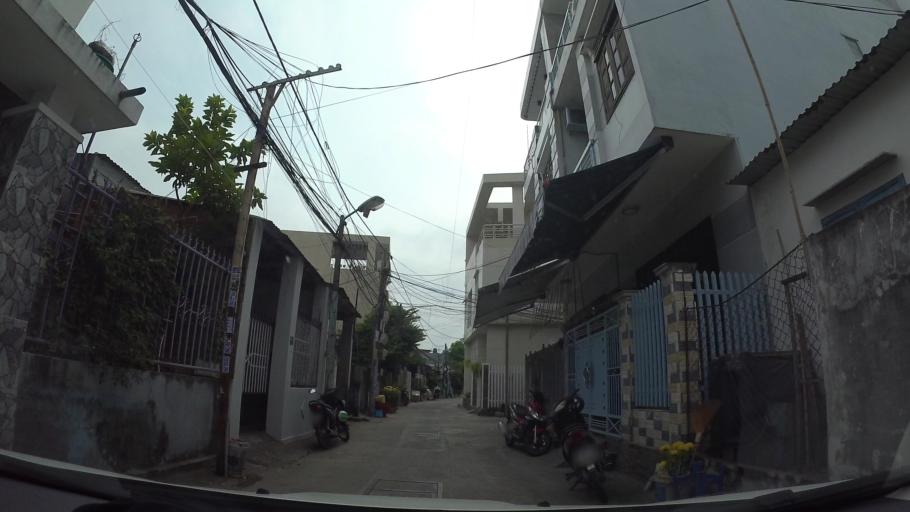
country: VN
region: Da Nang
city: Son Tra
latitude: 16.0951
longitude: 108.2457
